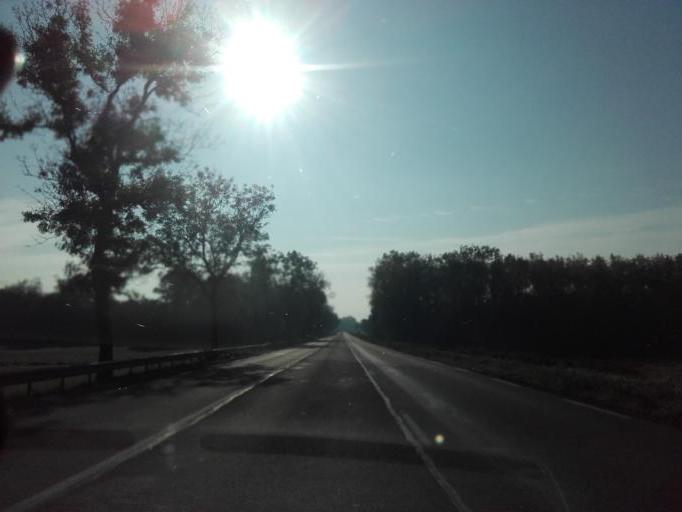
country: FR
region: Bourgogne
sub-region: Departement de Saone-et-Loire
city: Fontaines
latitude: 46.8785
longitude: 4.7814
